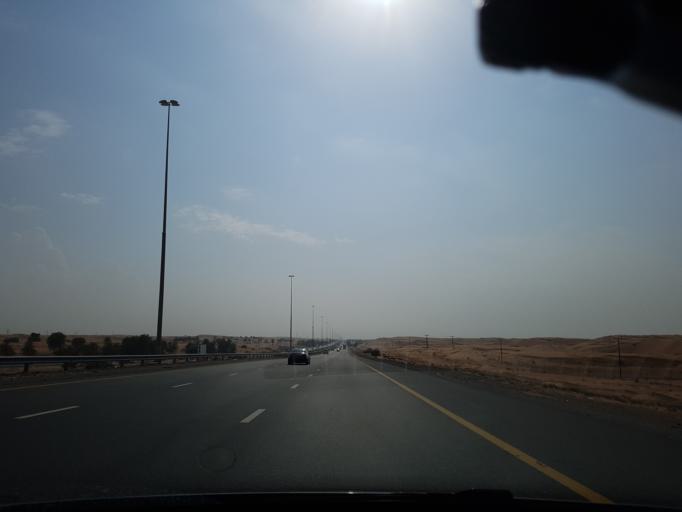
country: AE
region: Umm al Qaywayn
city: Umm al Qaywayn
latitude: 25.5171
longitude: 55.7106
